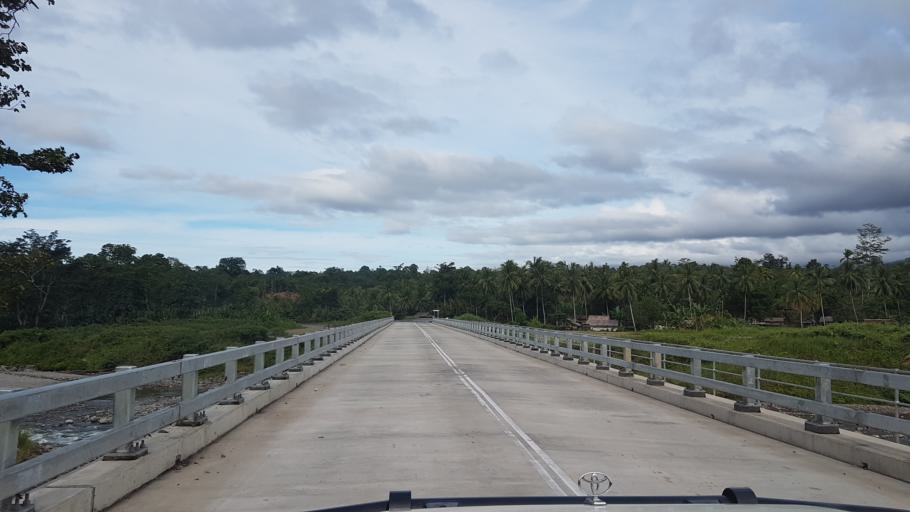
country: PG
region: Northern Province
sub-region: Sohe
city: Popondetta
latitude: -8.8366
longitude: 148.2701
